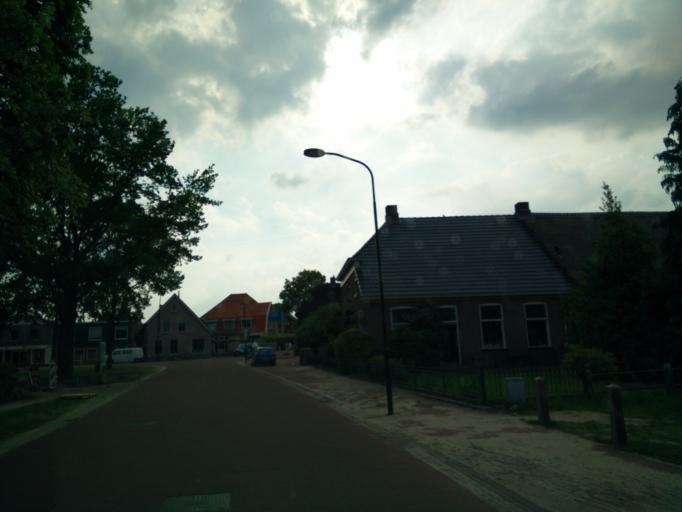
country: NL
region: Drenthe
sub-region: Gemeente Aa en Hunze
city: Anloo
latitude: 52.9871
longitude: 6.6492
